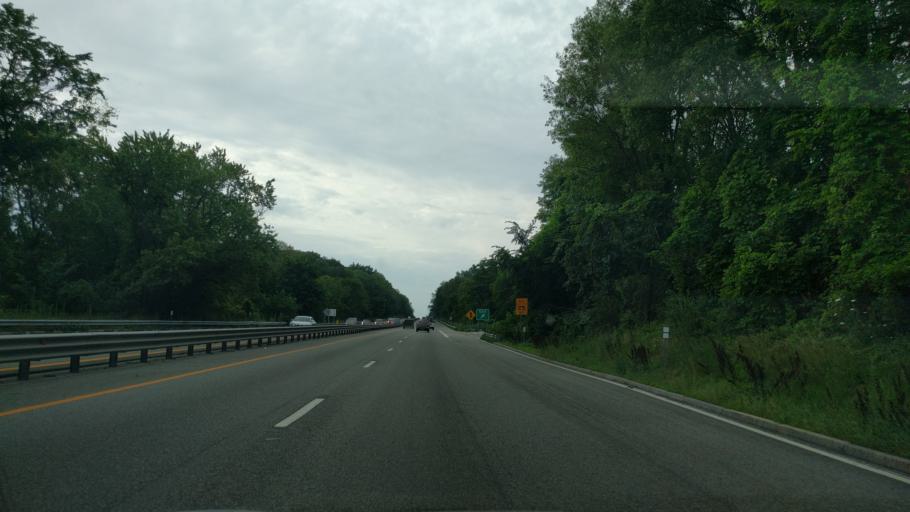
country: US
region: Rhode Island
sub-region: Providence County
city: Cumberland
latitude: 41.9228
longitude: -71.4569
